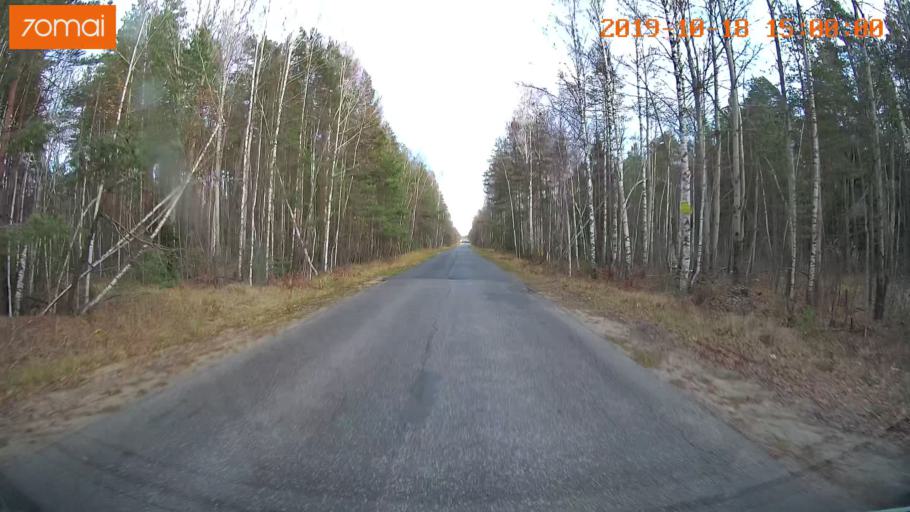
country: RU
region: Vladimir
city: Kurlovo
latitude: 55.4976
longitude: 40.5758
